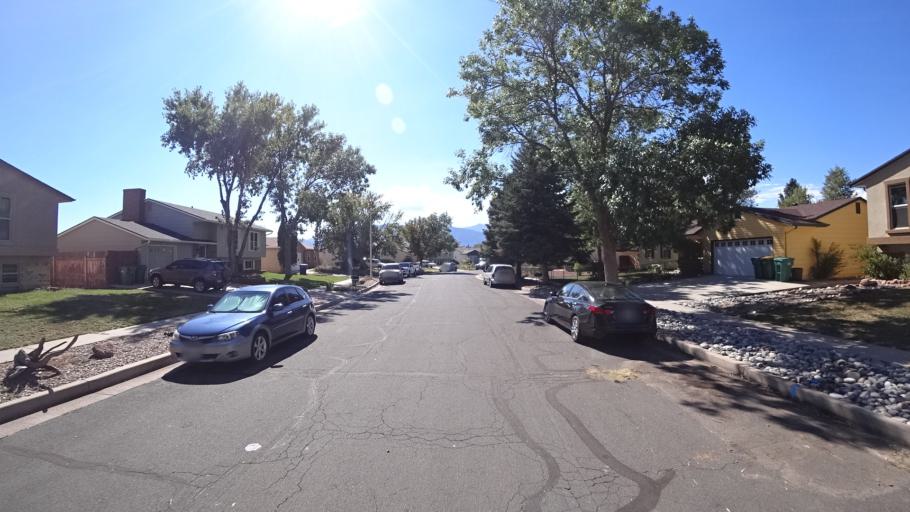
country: US
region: Colorado
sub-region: El Paso County
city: Stratmoor
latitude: 38.7907
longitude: -104.7452
